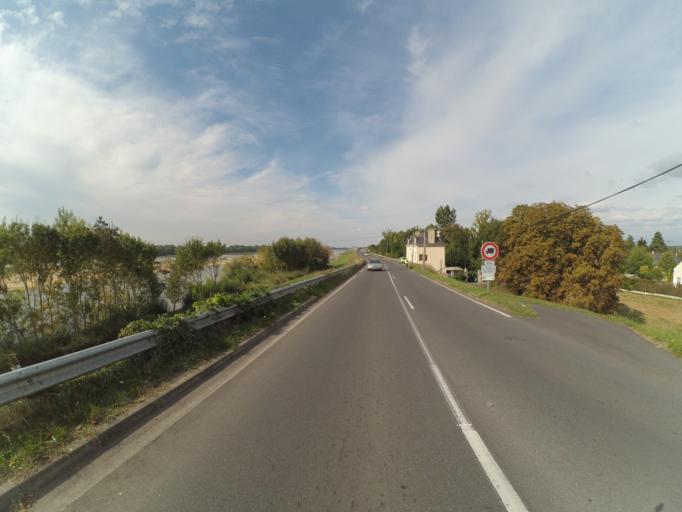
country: FR
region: Pays de la Loire
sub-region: Departement de Maine-et-Loire
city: Varennes-sur-Loire
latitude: 47.2277
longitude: 0.0498
